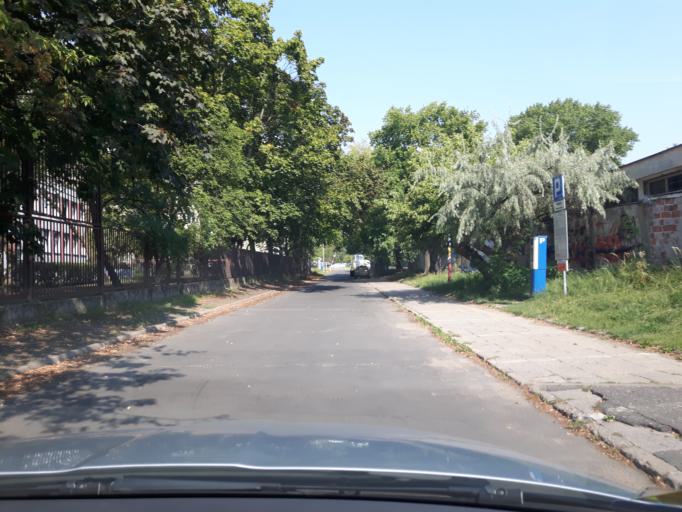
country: PL
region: Masovian Voivodeship
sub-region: Warszawa
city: Praga Polnoc
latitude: 52.2654
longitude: 21.0329
